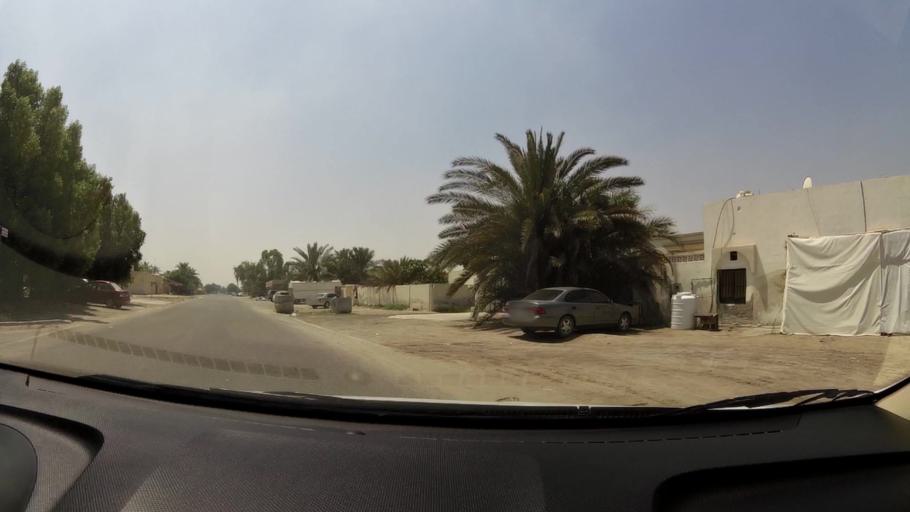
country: AE
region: Umm al Qaywayn
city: Umm al Qaywayn
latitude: 25.5616
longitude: 55.5562
